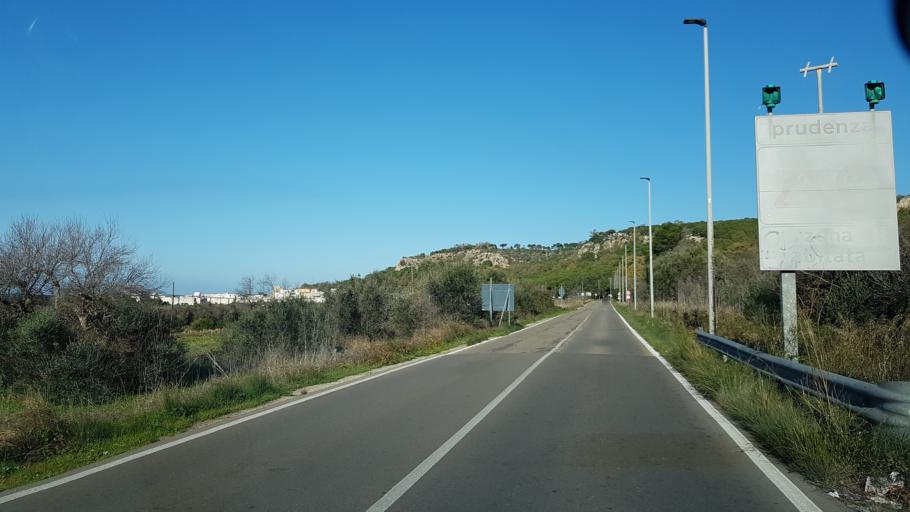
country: IT
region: Apulia
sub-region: Provincia di Lecce
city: Sannicola
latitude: 40.1037
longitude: 18.0193
